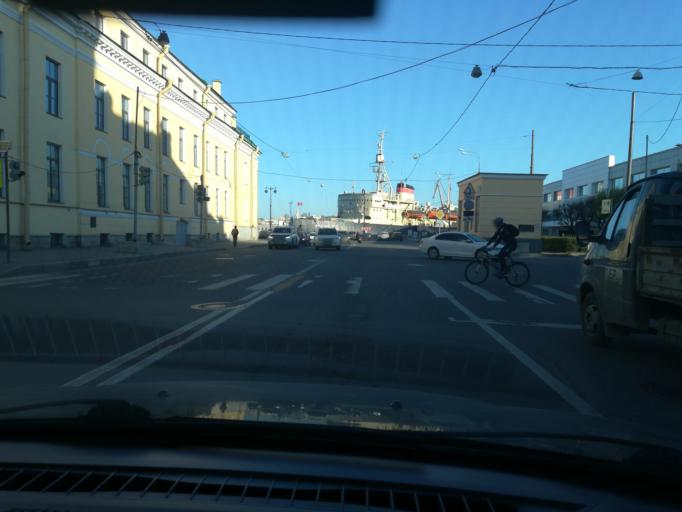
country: RU
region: St.-Petersburg
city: Vasyl'evsky Ostrov
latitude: 59.9292
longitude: 30.2673
